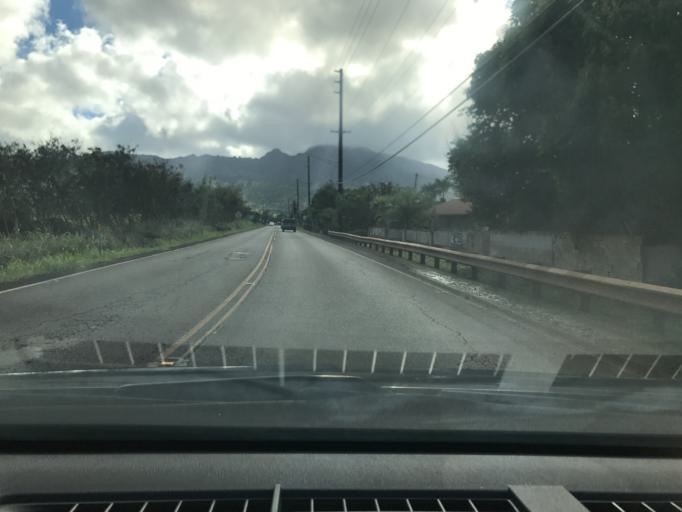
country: US
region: Hawaii
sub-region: Honolulu County
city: Hale'iwa
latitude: 21.5746
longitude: -158.1069
